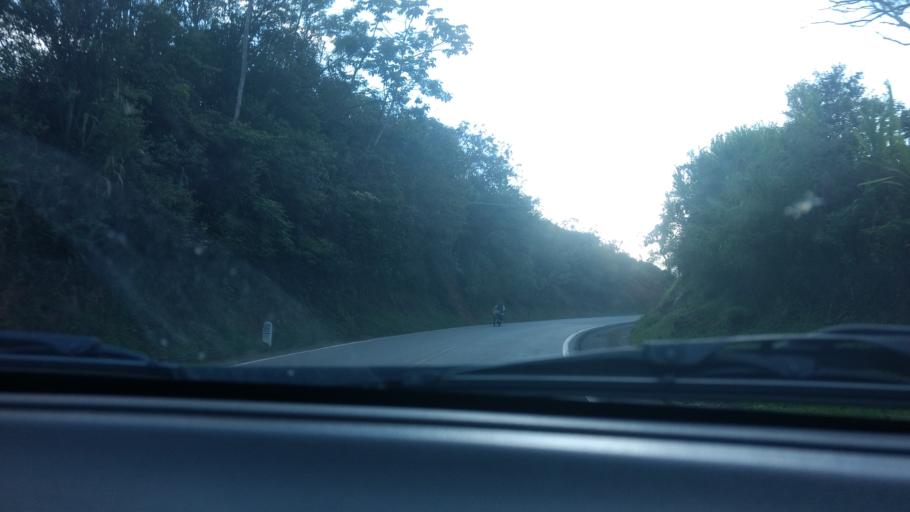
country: CO
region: Cauca
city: Rosas
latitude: 2.3354
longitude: -76.6918
